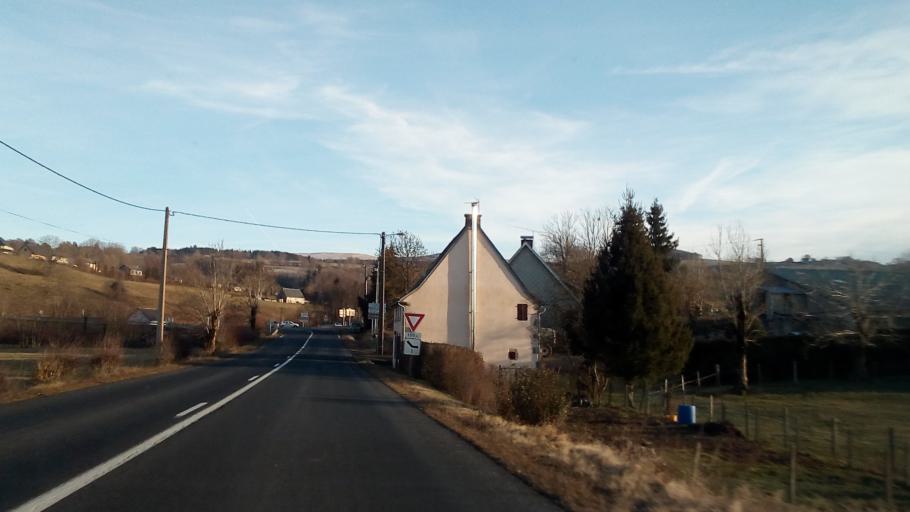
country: FR
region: Auvergne
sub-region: Departement du Puy-de-Dome
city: La Bourboule
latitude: 45.6427
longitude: 2.7220
